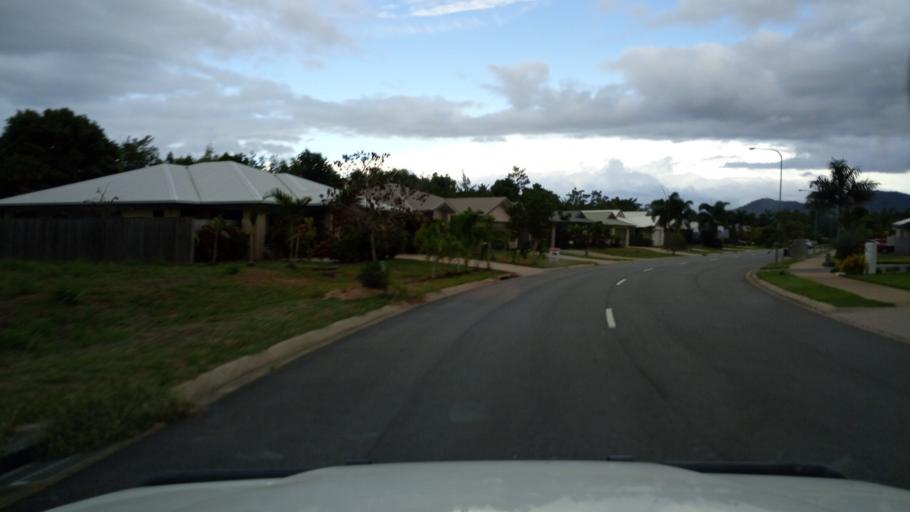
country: AU
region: Queensland
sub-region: Cairns
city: Redlynch
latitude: -16.8425
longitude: 145.6926
